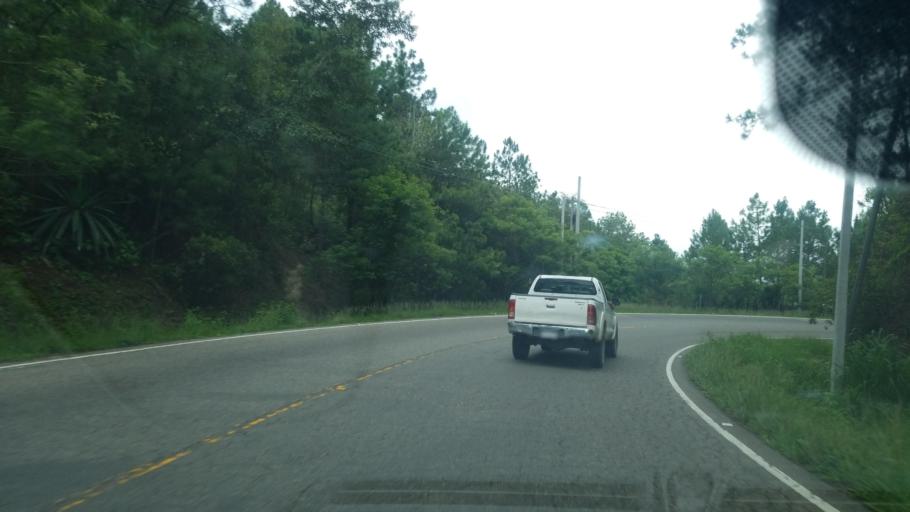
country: HN
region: Ocotepeque
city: Sinuapa
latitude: 14.4592
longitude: -89.1568
